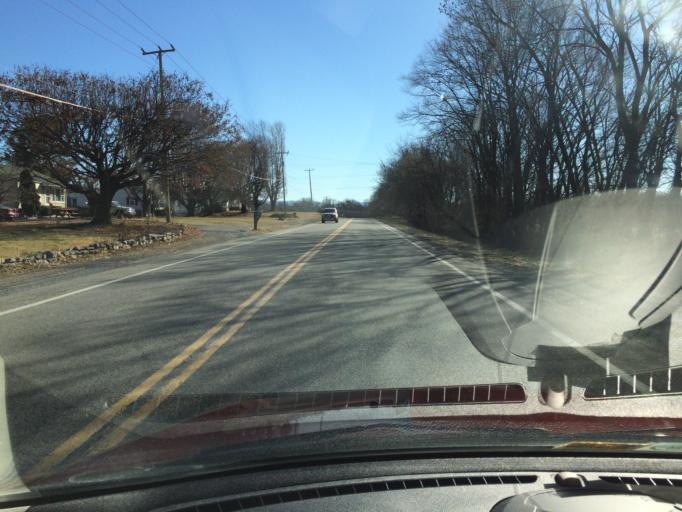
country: US
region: Virginia
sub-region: Rockingham County
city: Bridgewater
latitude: 38.3511
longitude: -78.9447
